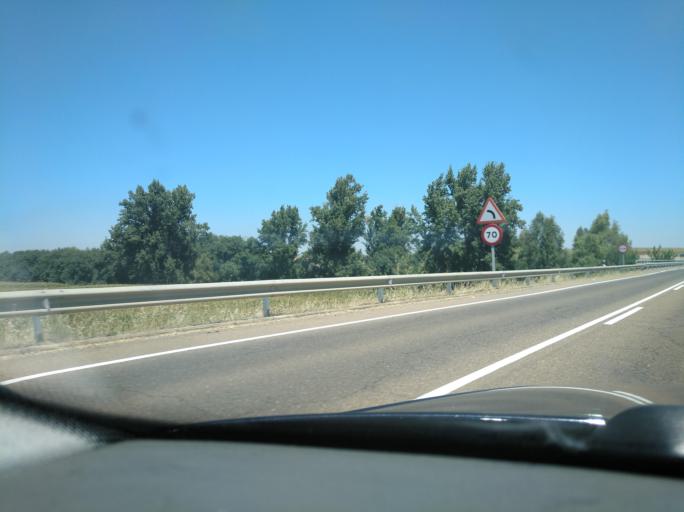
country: ES
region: Extremadura
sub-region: Provincia de Badajoz
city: Olivenza
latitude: 38.7411
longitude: -7.0640
